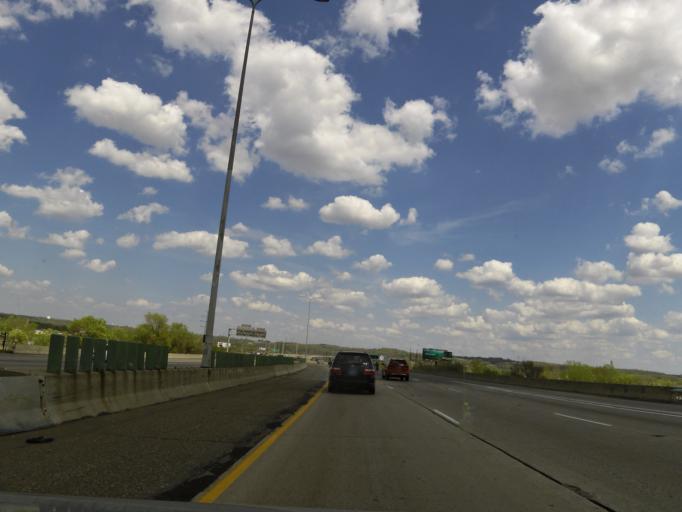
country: US
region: Minnesota
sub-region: Dakota County
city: South Saint Paul
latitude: 44.8756
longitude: -93.0316
